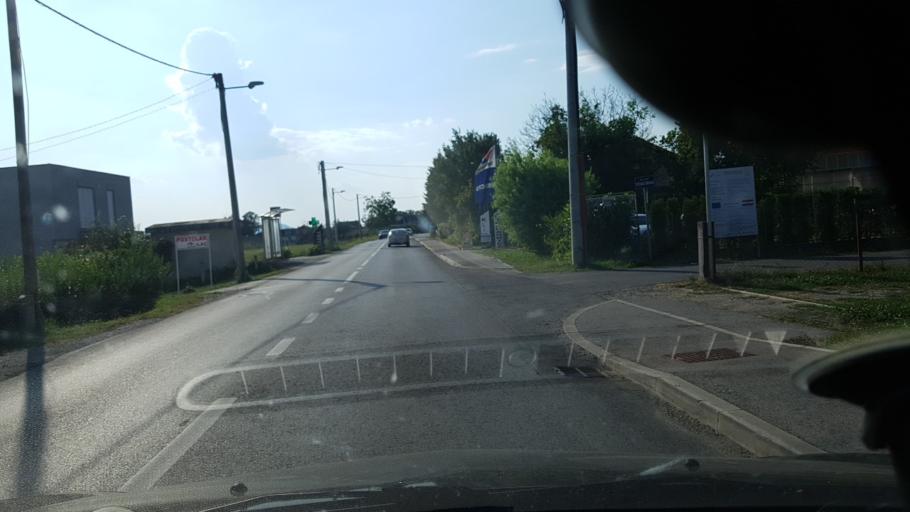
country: HR
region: Zagrebacka
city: Brdovec
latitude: 45.8795
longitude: 15.7285
